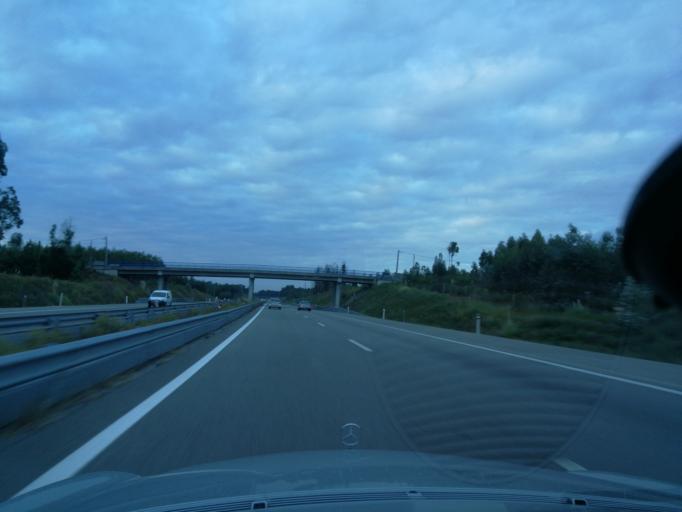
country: PT
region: Aveiro
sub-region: Estarreja
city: Salreu
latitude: 40.7091
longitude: -8.5329
